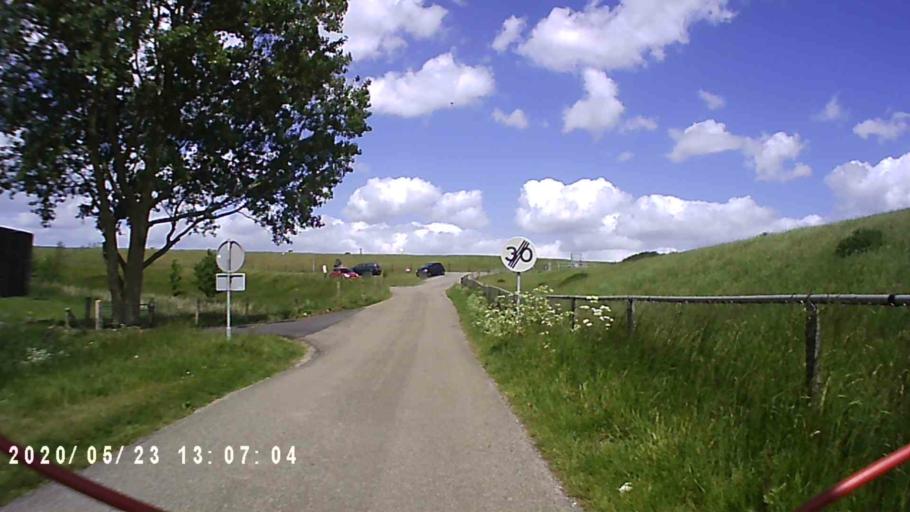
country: DE
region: Lower Saxony
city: Emden
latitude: 53.2988
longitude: 7.0753
